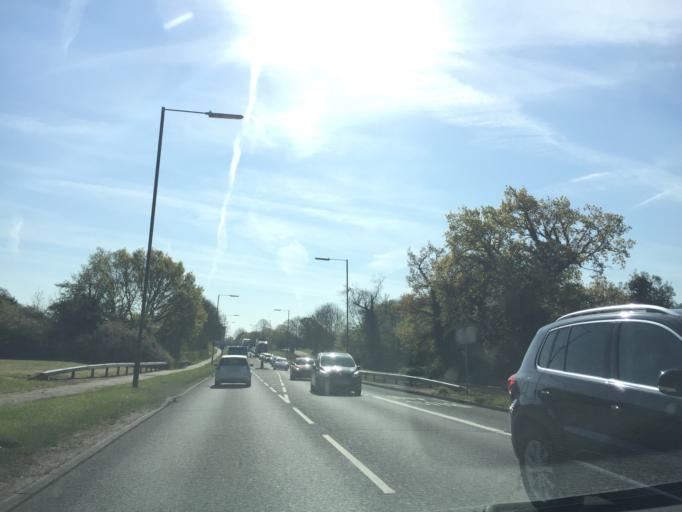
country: GB
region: England
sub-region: Essex
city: Harlow
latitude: 51.7658
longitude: 0.1076
